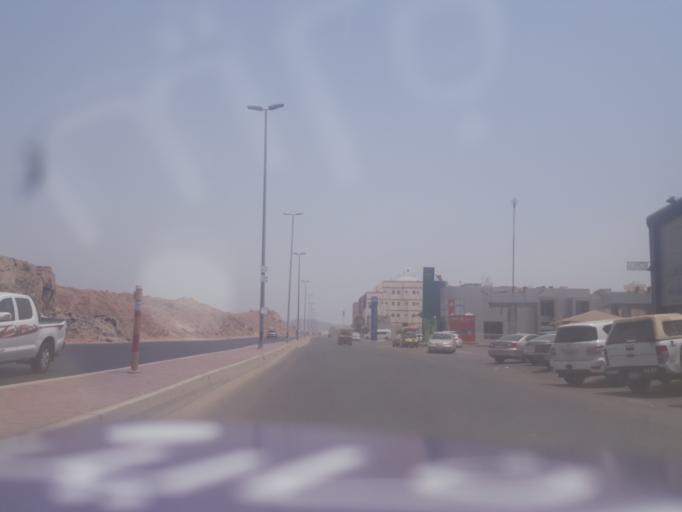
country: SA
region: Makkah
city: Jeddah
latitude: 21.4020
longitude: 39.2770
